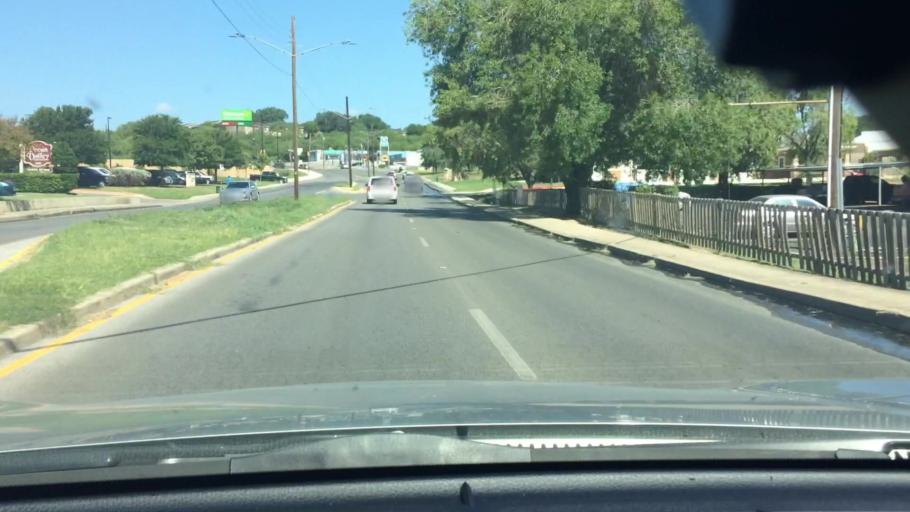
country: US
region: Texas
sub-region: Bexar County
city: San Antonio
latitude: 29.3758
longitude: -98.4301
